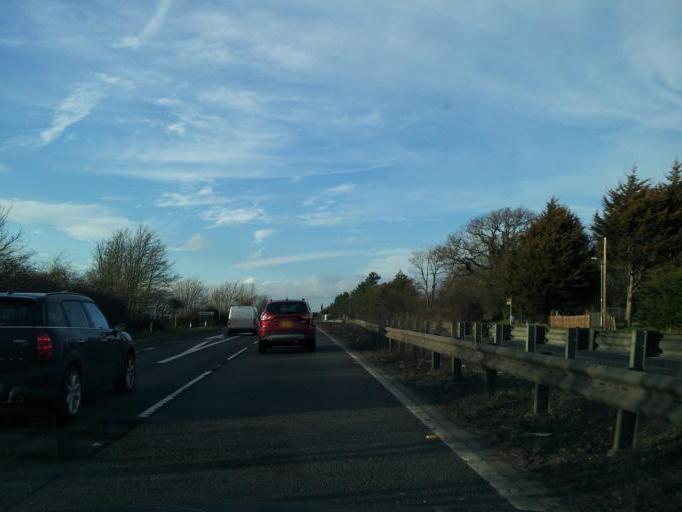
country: GB
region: England
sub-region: Peterborough
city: Thornhaugh
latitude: 52.5917
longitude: -0.4175
